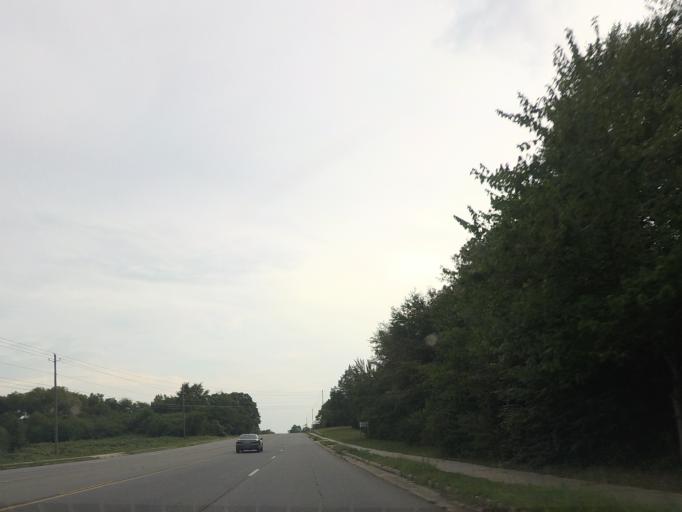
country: US
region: Georgia
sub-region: Houston County
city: Centerville
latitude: 32.7287
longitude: -83.6825
